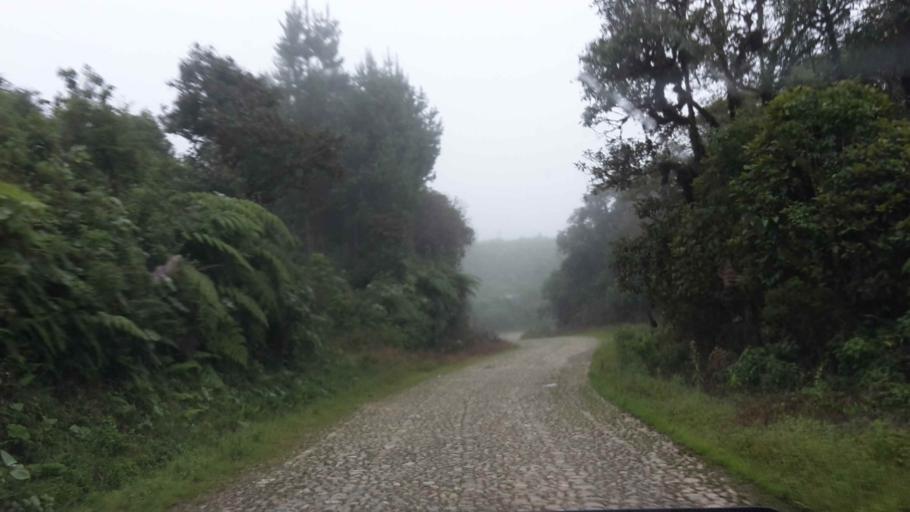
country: BO
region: Cochabamba
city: Colomi
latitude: -17.1192
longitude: -65.9628
